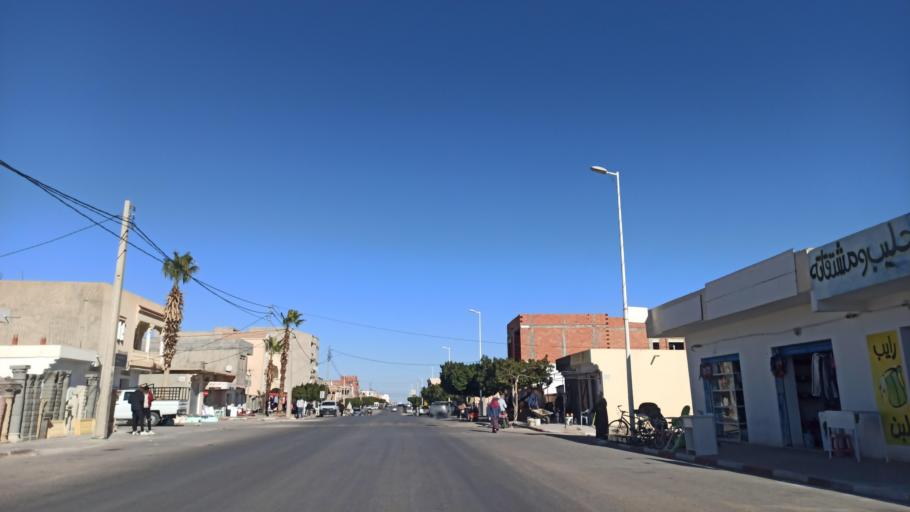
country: TN
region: Sidi Bu Zayd
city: Bi'r al Hufayy
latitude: 34.9365
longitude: 9.1995
